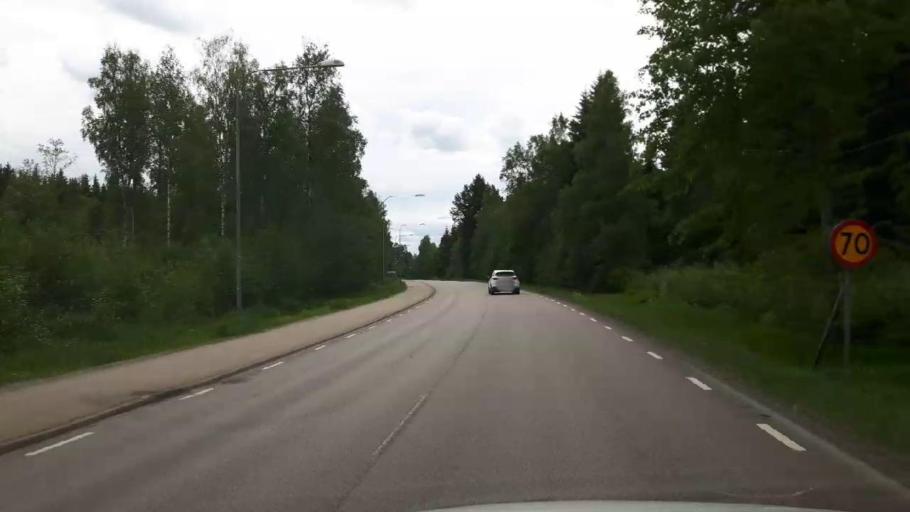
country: SE
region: Vaestmanland
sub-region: Norbergs Kommun
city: Norberg
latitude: 60.0875
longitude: 15.9356
